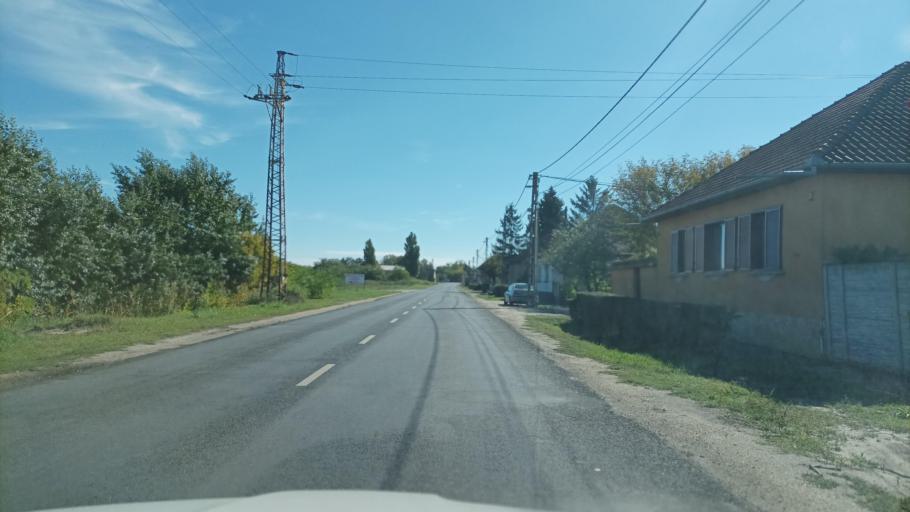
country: HU
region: Pest
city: Cegled
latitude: 47.1703
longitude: 19.8227
